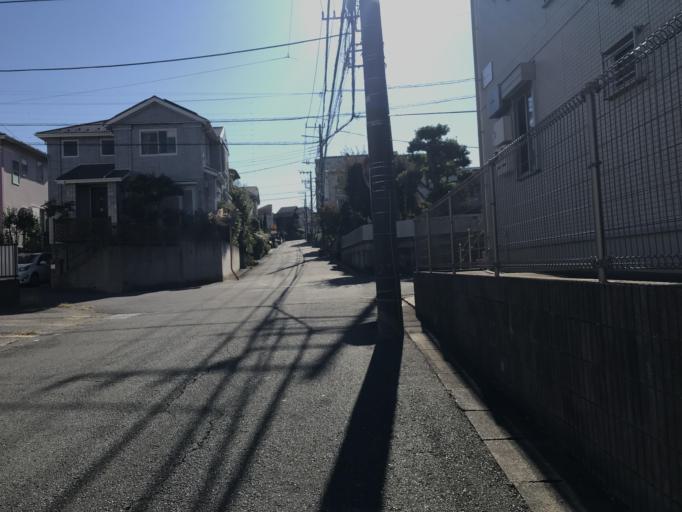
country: JP
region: Tokyo
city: Chofugaoka
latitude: 35.5705
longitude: 139.5862
